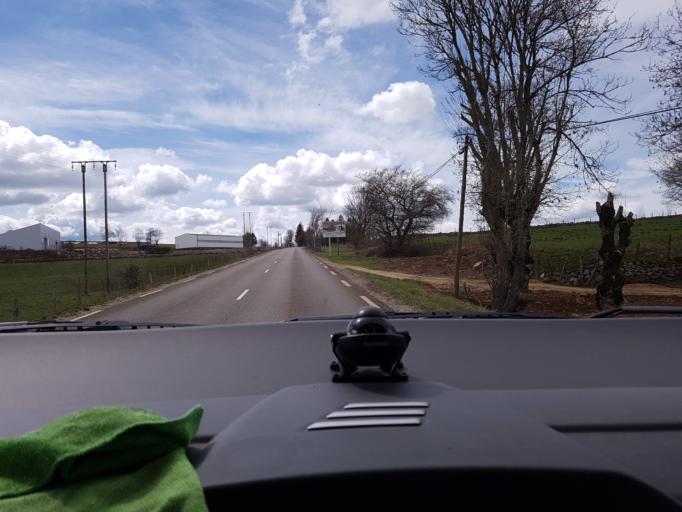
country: FR
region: Midi-Pyrenees
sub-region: Departement de l'Aveyron
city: Laguiole
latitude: 44.7737
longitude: 2.8914
